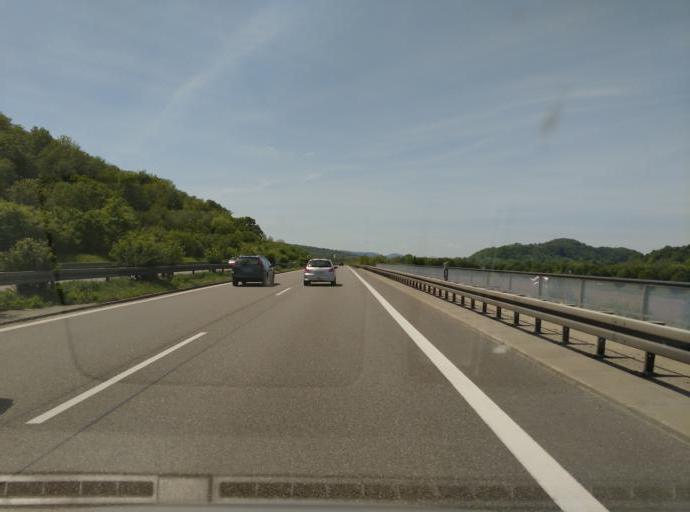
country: DE
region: Baden-Wuerttemberg
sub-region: Tuebingen Region
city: Kusterdingen
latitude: 48.5321
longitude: 9.1106
